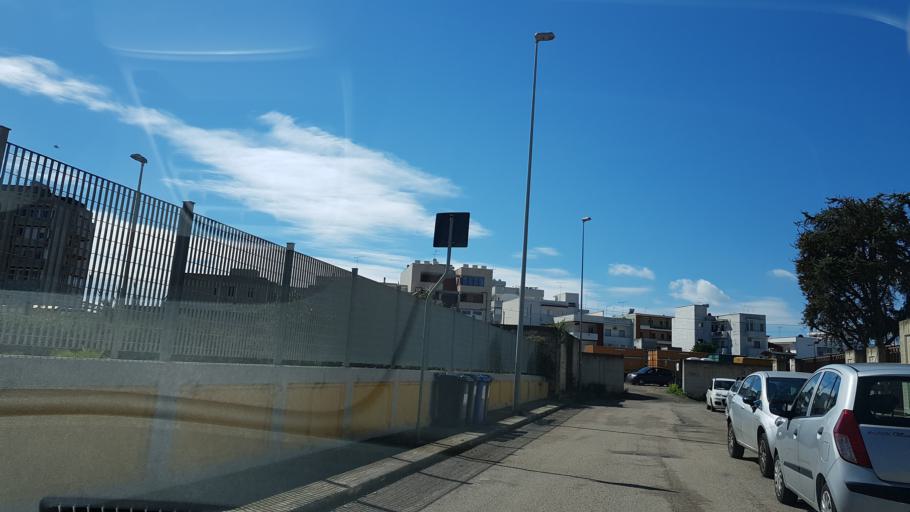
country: IT
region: Apulia
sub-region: Provincia di Brindisi
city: Brindisi
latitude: 40.6358
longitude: 17.9260
